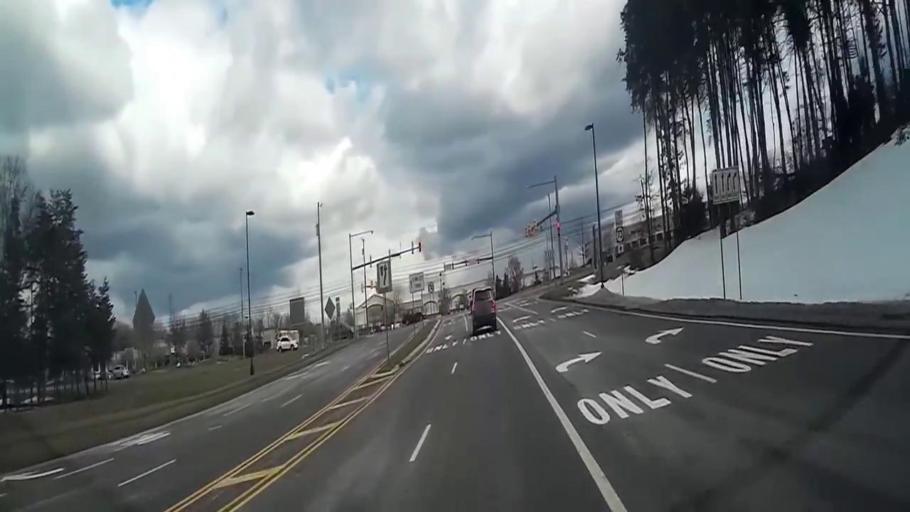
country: US
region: New Jersey
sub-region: Camden County
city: Gibbsboro
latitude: 39.8358
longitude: -74.9268
